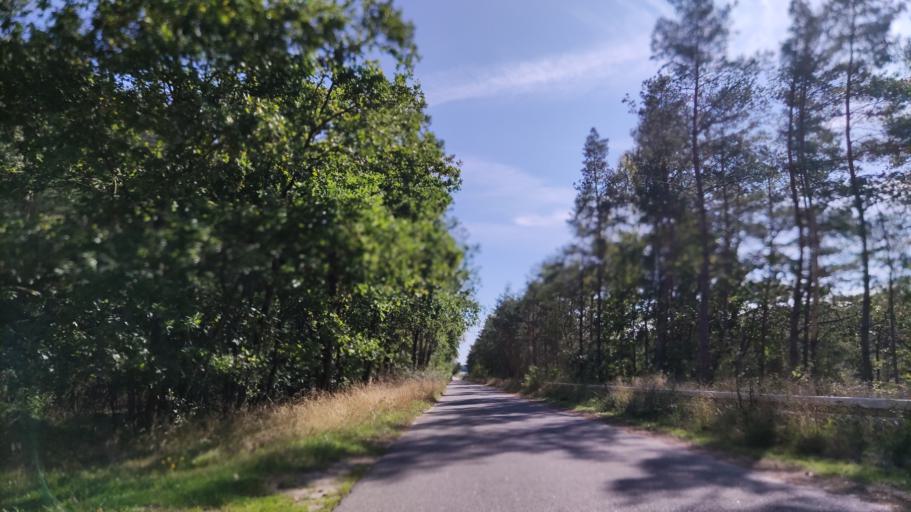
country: DE
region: Lower Saxony
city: Wendisch Evern
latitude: 53.2122
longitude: 10.4957
